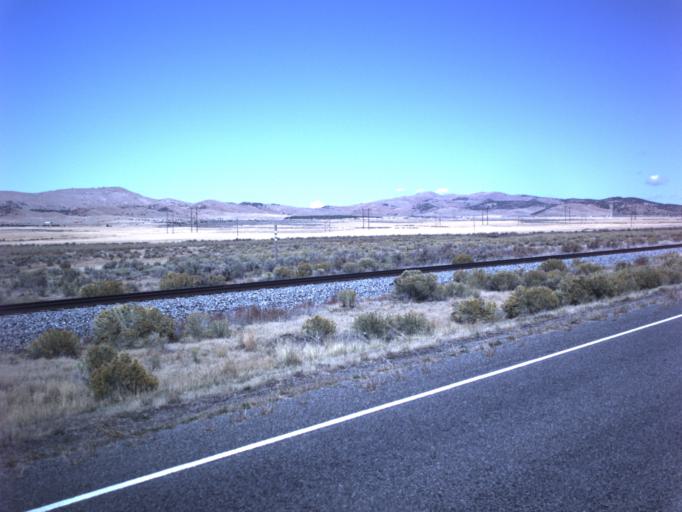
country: US
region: Utah
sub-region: Juab County
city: Nephi
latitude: 39.5393
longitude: -111.9287
